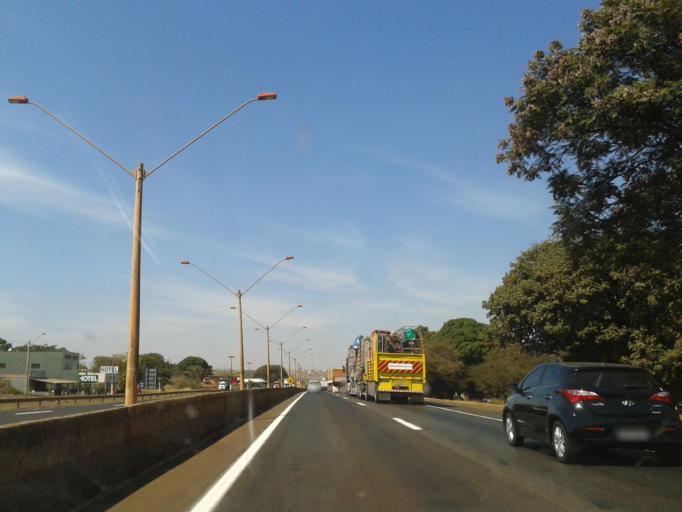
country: BR
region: Goias
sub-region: Itumbiara
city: Itumbiara
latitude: -18.4088
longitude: -49.1973
